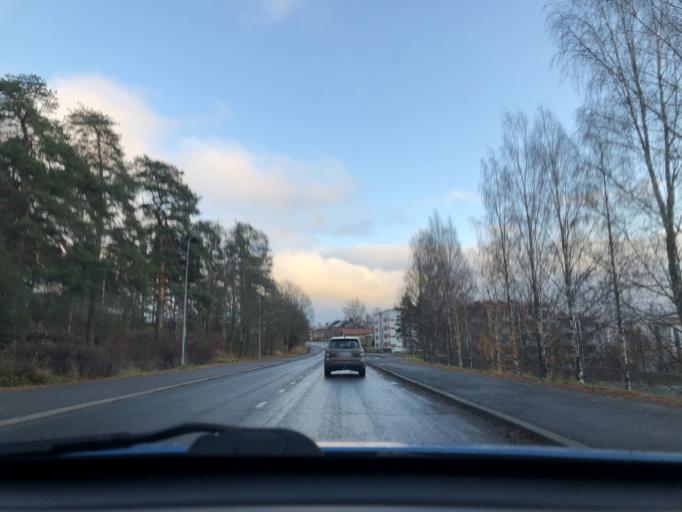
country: FI
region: Pirkanmaa
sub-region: Tampere
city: Kangasala
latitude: 61.4650
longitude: 24.0571
